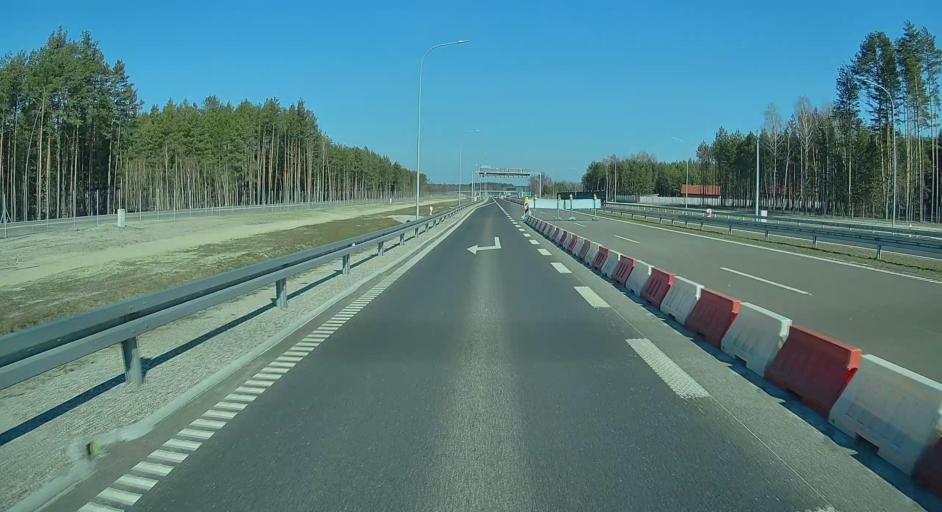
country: PL
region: Subcarpathian Voivodeship
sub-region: Powiat nizanski
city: Jarocin
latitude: 50.5769
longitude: 22.2508
